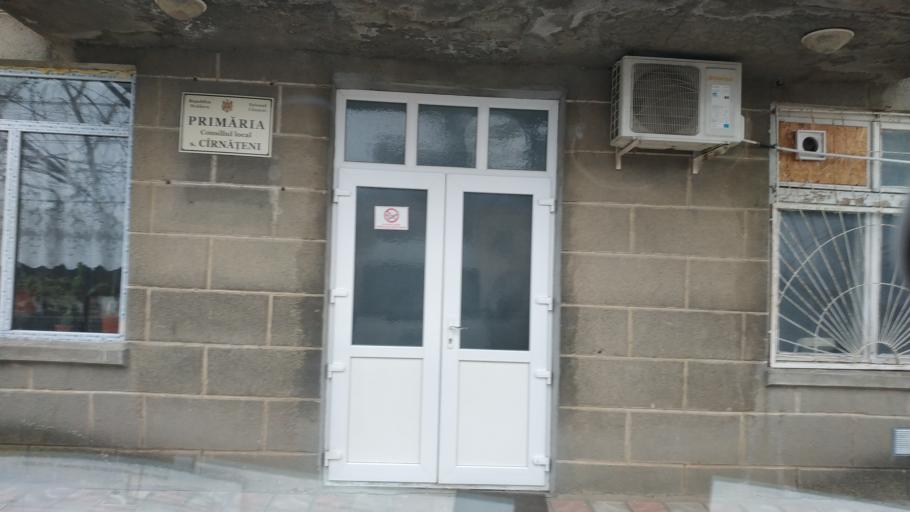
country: MD
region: Causeni
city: Causeni
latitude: 46.6632
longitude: 29.4883
